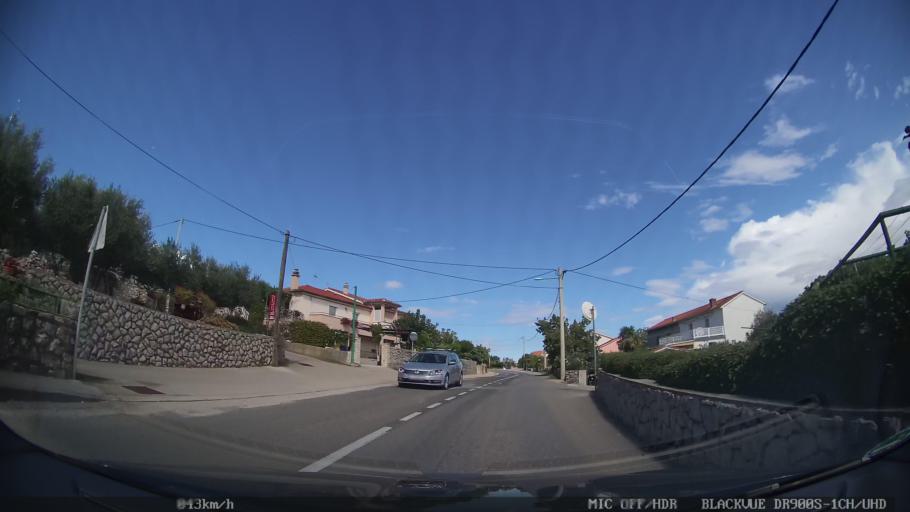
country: HR
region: Primorsko-Goranska
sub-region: Grad Krk
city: Krk
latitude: 45.0450
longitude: 14.5419
